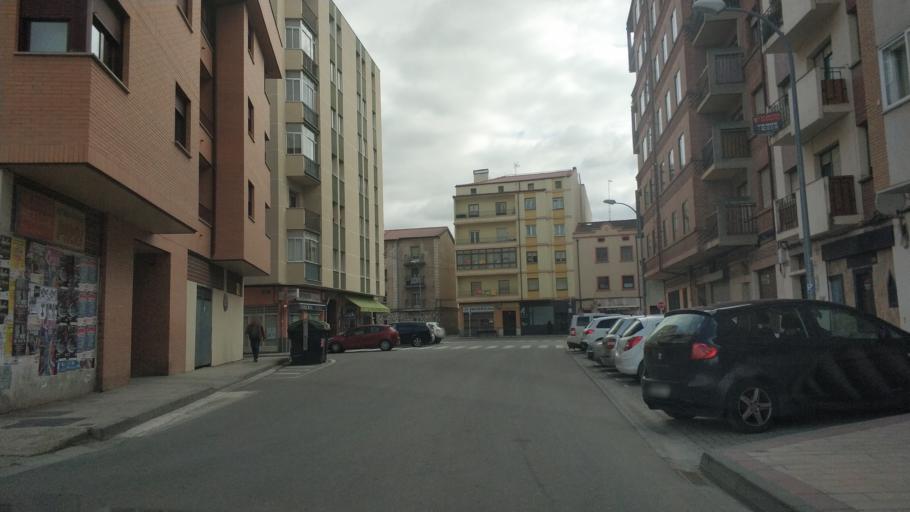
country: ES
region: Castille and Leon
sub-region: Provincia de Burgos
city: Aranda de Duero
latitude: 41.6727
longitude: -3.6814
